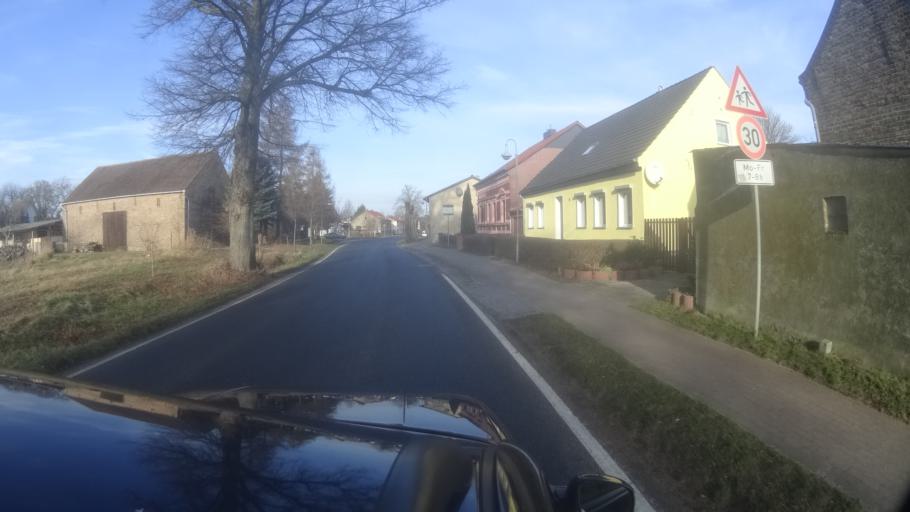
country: DE
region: Brandenburg
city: Kremmen
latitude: 52.8136
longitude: 13.0197
